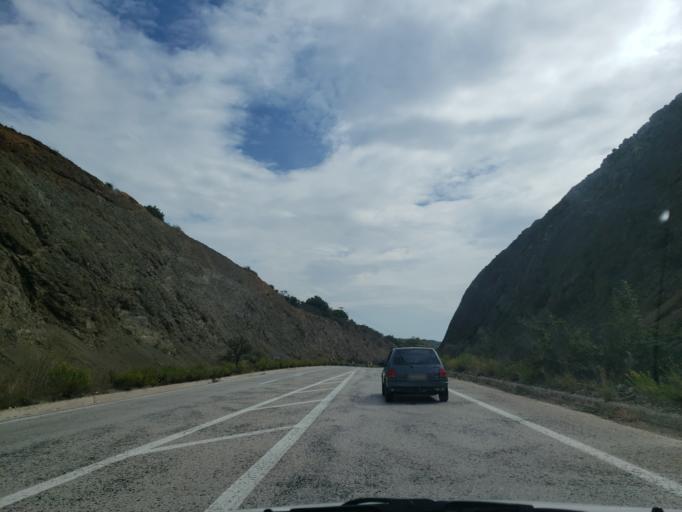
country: GR
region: Central Greece
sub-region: Nomos Fthiotidos
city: Stavros
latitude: 38.9882
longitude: 22.3758
